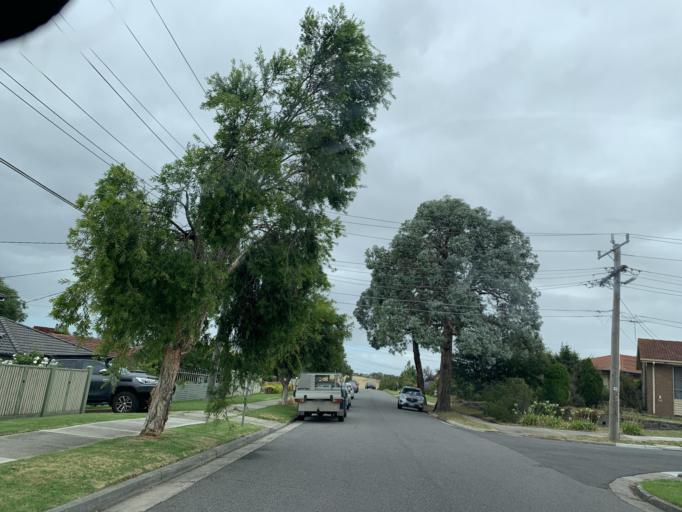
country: AU
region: Victoria
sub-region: Hume
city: Jacana
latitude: -37.6828
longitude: 144.9099
